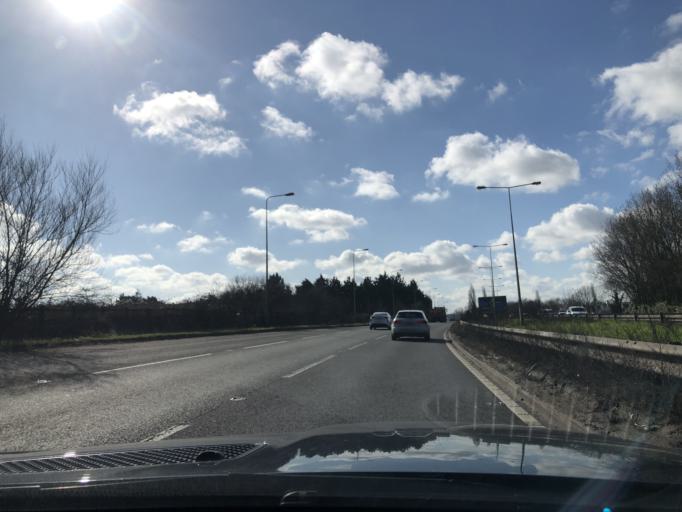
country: GB
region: England
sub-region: Northamptonshire
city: Hardingstone
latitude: 52.1916
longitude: -0.8926
